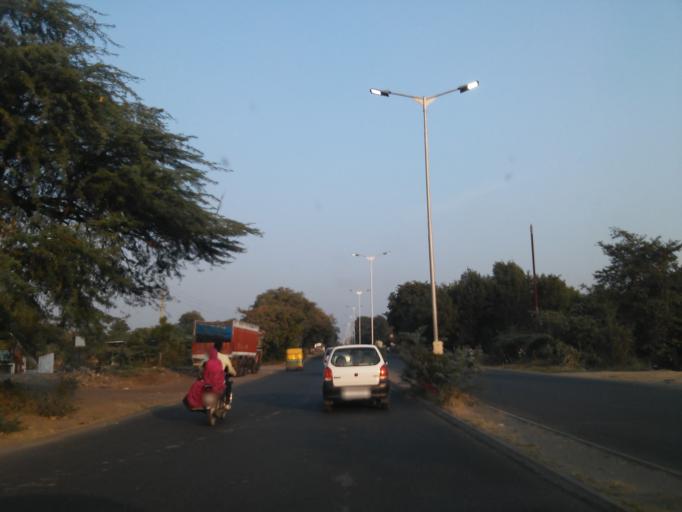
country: IN
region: Gujarat
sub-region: Ahmadabad
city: Sarkhej
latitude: 22.9877
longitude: 72.4769
